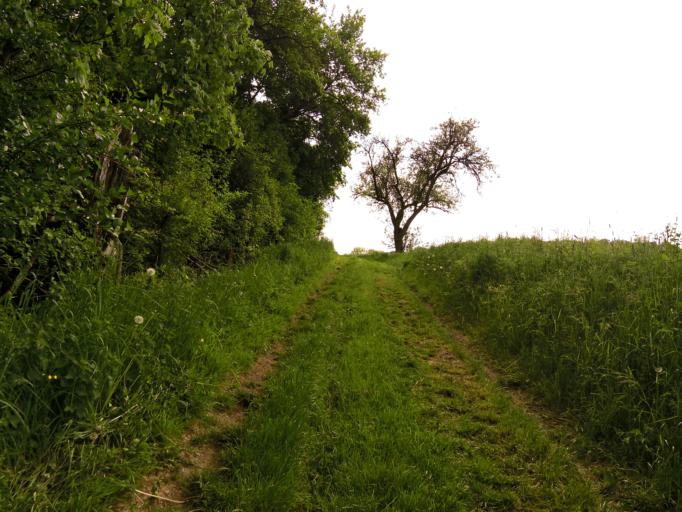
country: DE
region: Thuringia
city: Ifta
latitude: 51.0604
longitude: 10.1619
